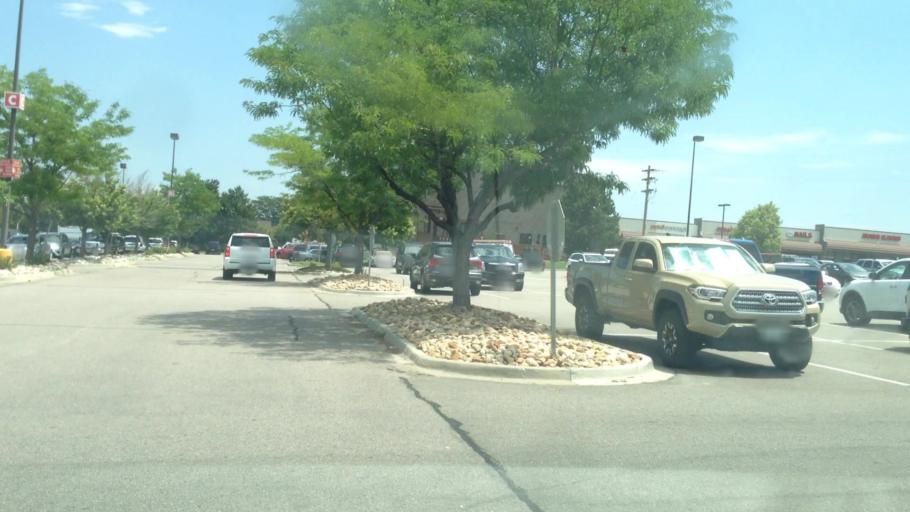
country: US
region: Colorado
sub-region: Arapahoe County
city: Centennial
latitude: 39.5963
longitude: -104.8795
